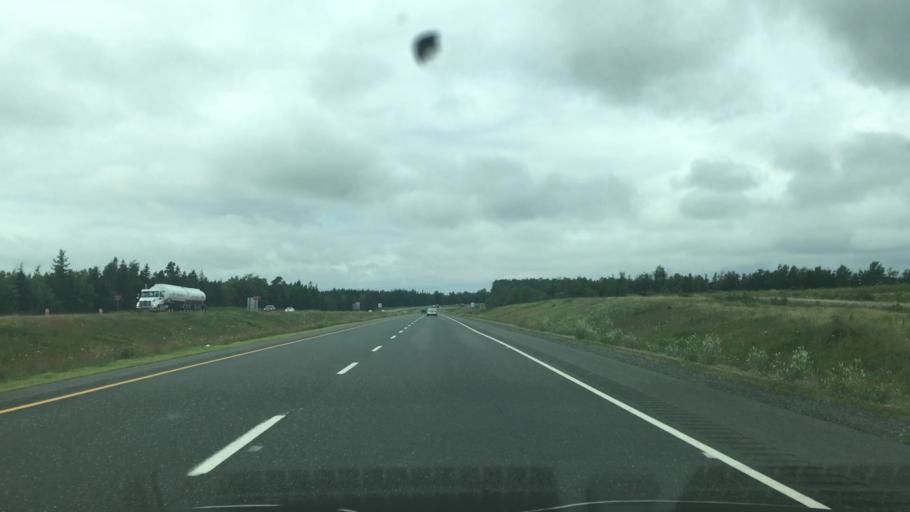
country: CA
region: Nova Scotia
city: Truro
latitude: 45.3844
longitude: -63.3451
